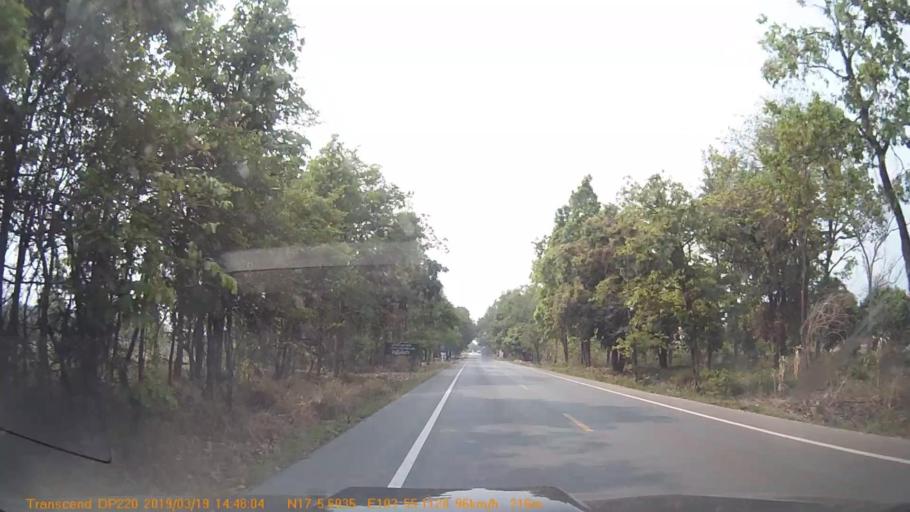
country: TH
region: Sakon Nakhon
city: Kut Bak
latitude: 17.0936
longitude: 103.9183
